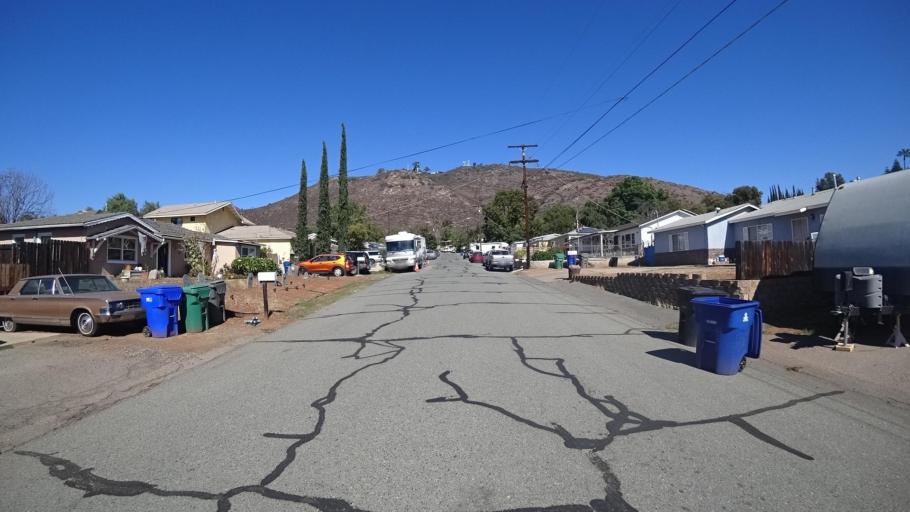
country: US
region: California
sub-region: San Diego County
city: Winter Gardens
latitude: 32.8229
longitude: -116.9455
